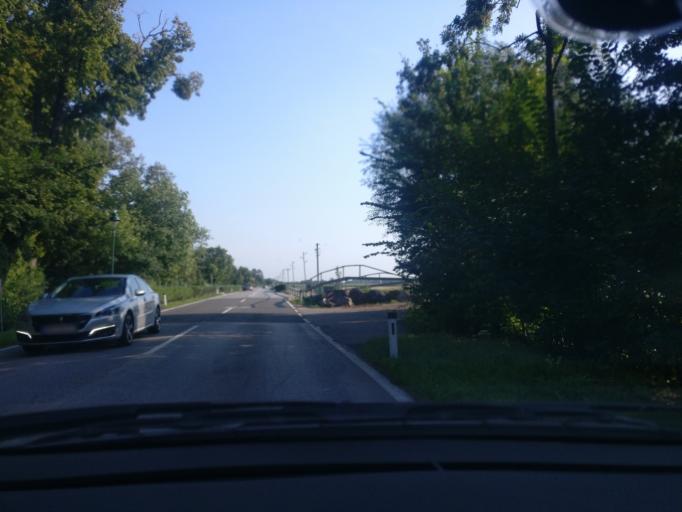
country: AT
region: Lower Austria
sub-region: Politischer Bezirk Modling
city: Laxenburg
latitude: 48.0614
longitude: 16.3530
